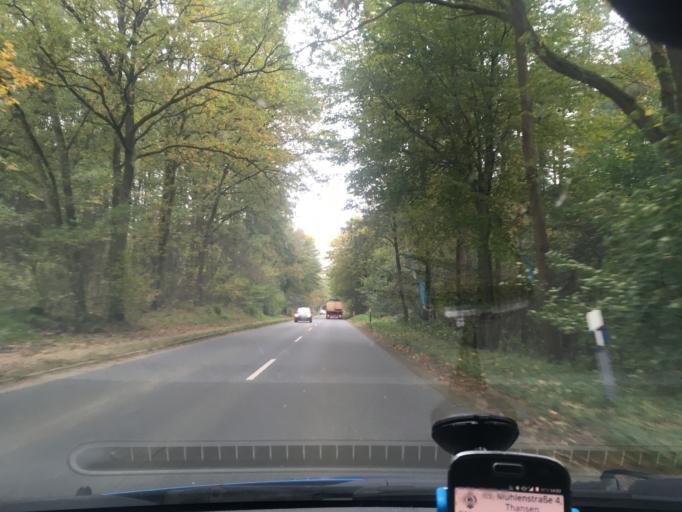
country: DE
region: Lower Saxony
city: Soderstorf
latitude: 53.1364
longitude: 10.1547
